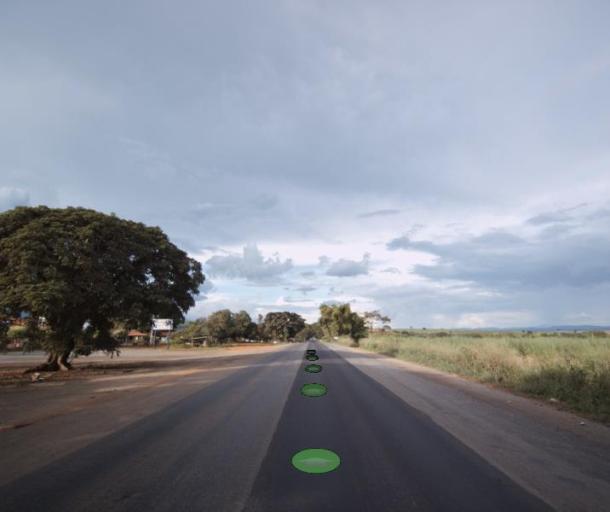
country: BR
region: Goias
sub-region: Itapaci
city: Itapaci
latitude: -15.1201
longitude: -49.4997
